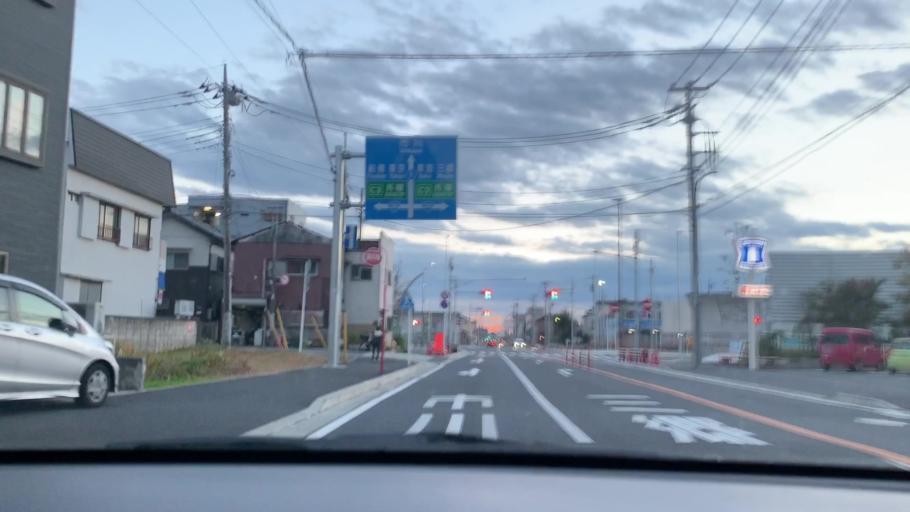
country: JP
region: Chiba
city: Matsudo
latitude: 35.7645
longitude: 139.8994
